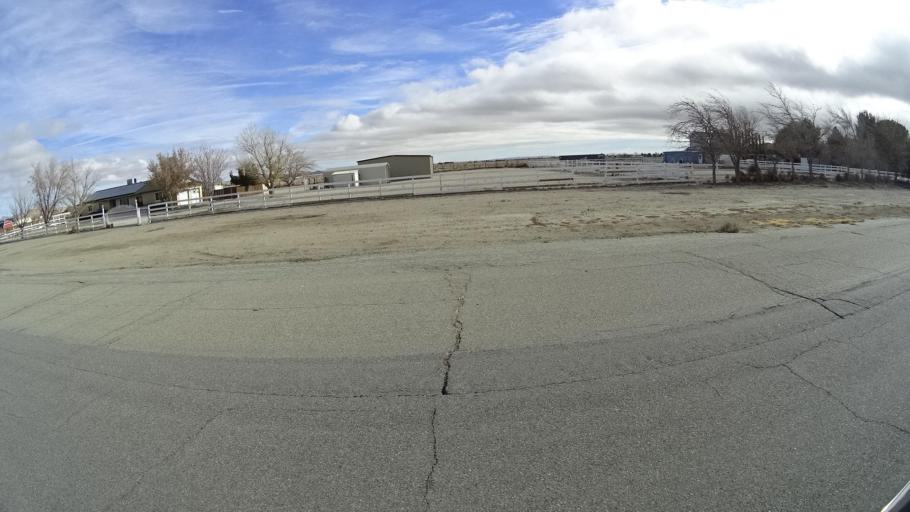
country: US
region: California
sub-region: Kern County
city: Rosamond
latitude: 34.8303
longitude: -118.2730
